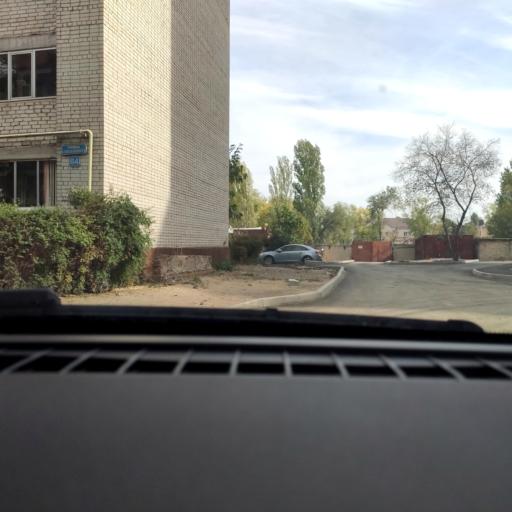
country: RU
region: Voronezj
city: Voronezh
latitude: 51.7121
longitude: 39.2728
